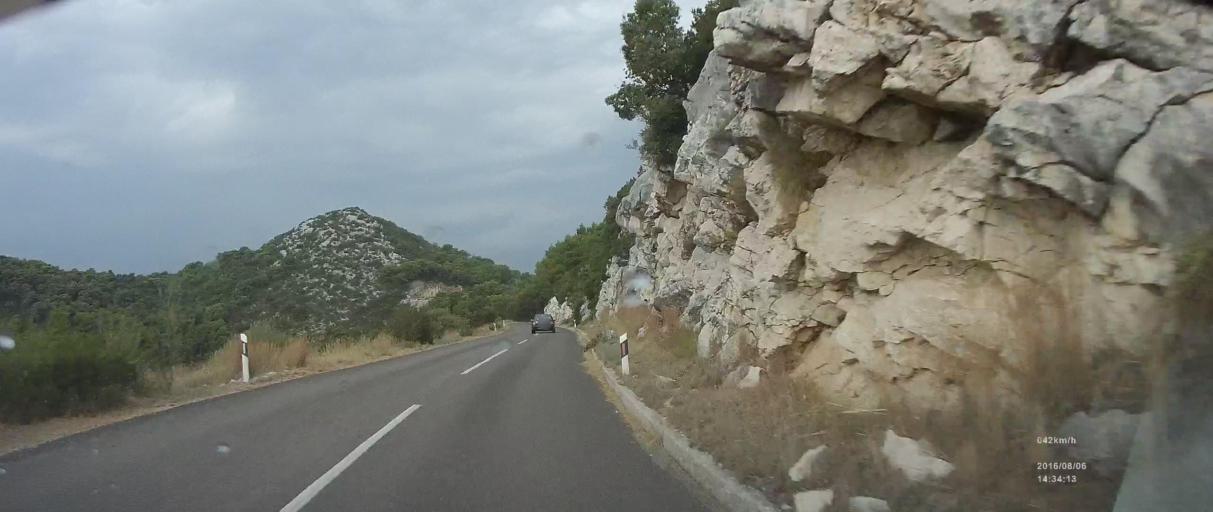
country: HR
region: Dubrovacko-Neretvanska
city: Ston
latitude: 42.7117
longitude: 17.7000
